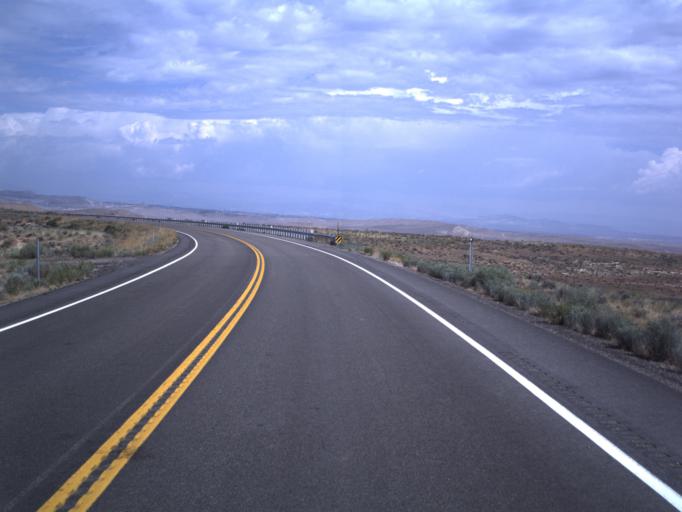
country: US
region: Utah
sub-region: Uintah County
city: Naples
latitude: 40.2582
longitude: -109.4334
